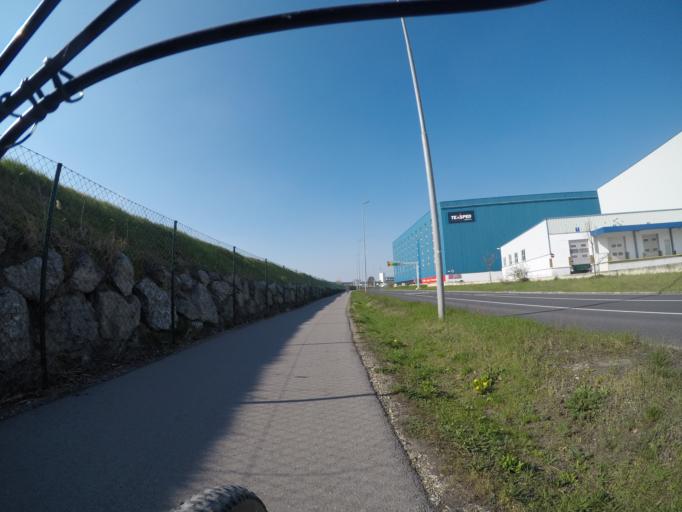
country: AT
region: Lower Austria
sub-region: Politischer Bezirk Modling
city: Neu-Guntramsdorf
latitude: 48.0600
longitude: 16.3363
